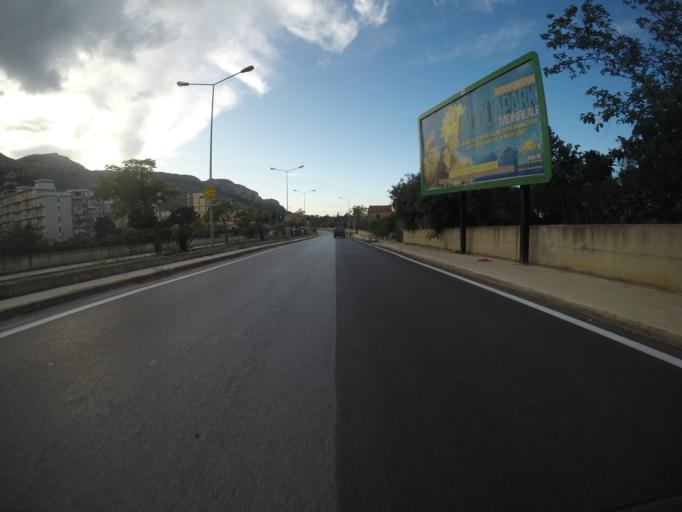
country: IT
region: Sicily
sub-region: Palermo
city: Isola delle Femmine
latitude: 38.1942
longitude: 13.2845
